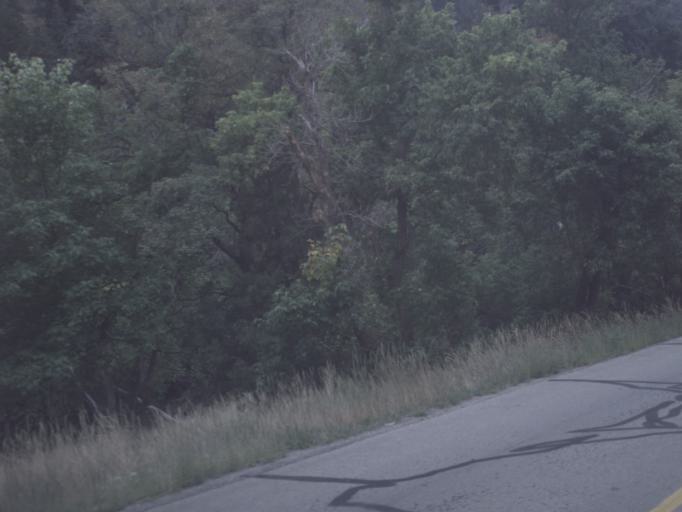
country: US
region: Utah
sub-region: Utah County
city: Cedar Hills
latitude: 40.4406
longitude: -111.7177
